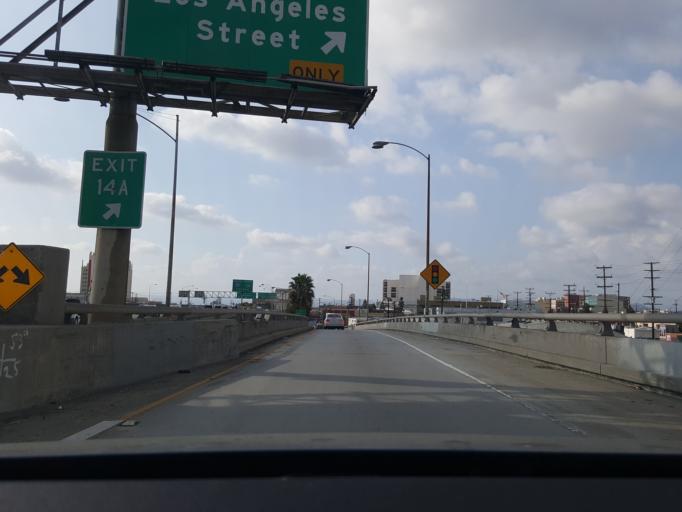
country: US
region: California
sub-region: Los Angeles County
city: Los Angeles
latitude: 34.0311
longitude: -118.2588
